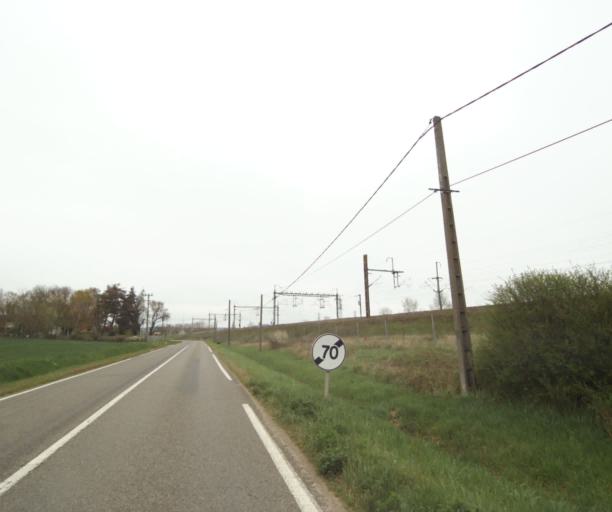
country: FR
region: Bourgogne
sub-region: Departement de Saone-et-Loire
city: Charnay-les-Macon
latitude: 46.2860
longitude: 4.7755
